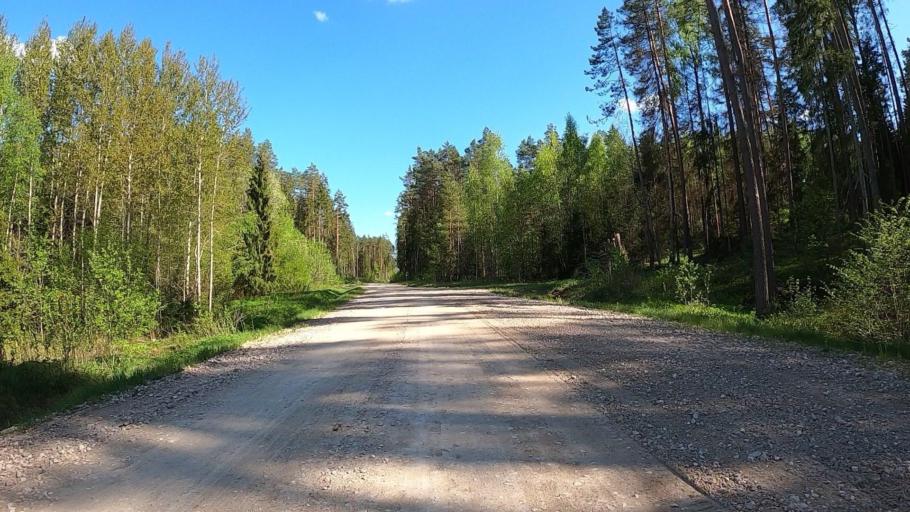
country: LV
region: Baldone
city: Baldone
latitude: 56.7667
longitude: 24.3789
